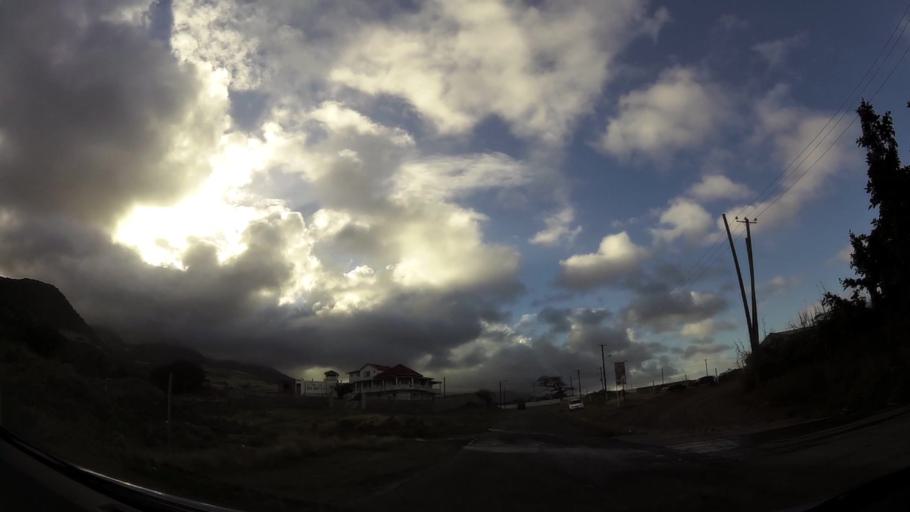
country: KN
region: Saint Mary Cayon
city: Cayon
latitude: 17.3480
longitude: -62.7255
